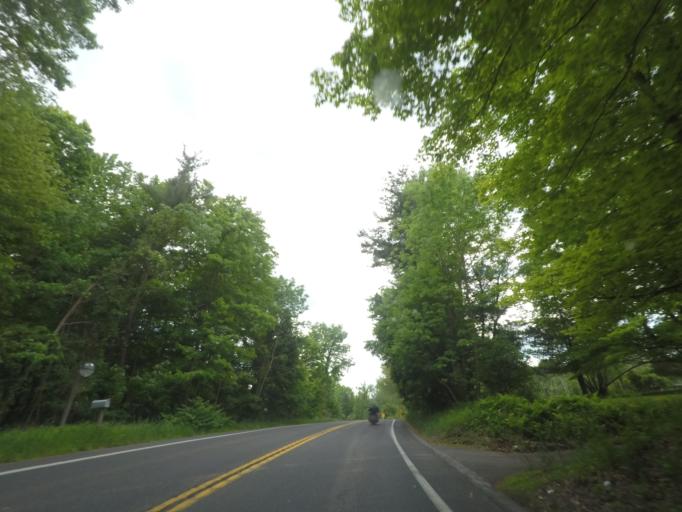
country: US
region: New York
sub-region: Dutchess County
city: Pine Plains
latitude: 42.0803
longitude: -73.6721
